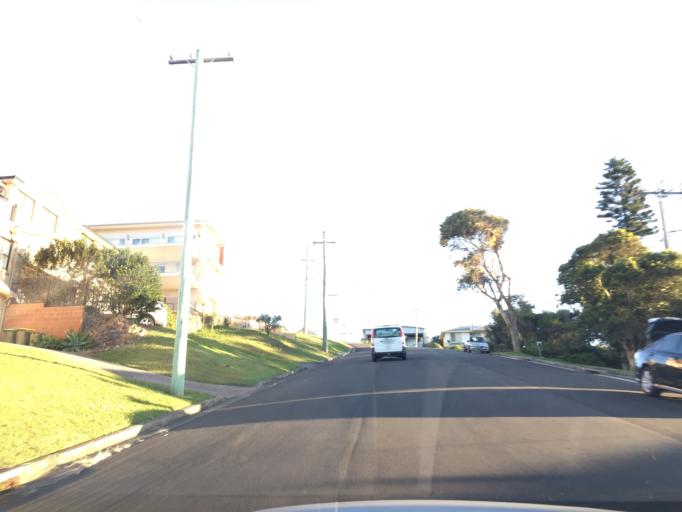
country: AU
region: New South Wales
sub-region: Kiama
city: Kiama
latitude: -34.6645
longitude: 150.8508
